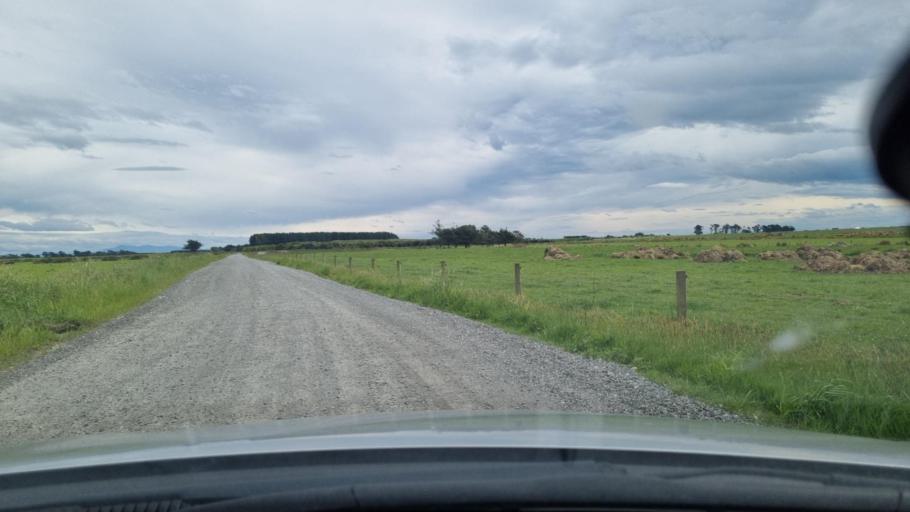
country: NZ
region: Southland
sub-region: Invercargill City
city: Invercargill
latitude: -46.4014
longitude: 168.2836
